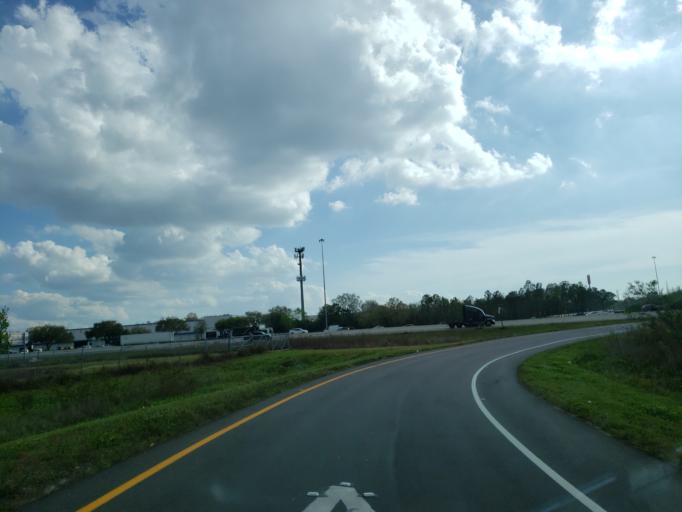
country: US
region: Florida
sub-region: Hillsborough County
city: East Lake-Orient Park
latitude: 27.9969
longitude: -82.3553
